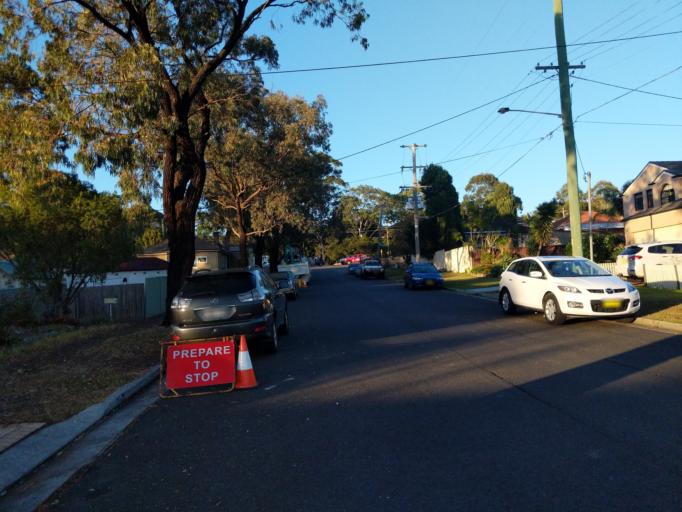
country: AU
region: New South Wales
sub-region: Sutherland Shire
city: Kirrawee
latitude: -34.0310
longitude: 151.0702
